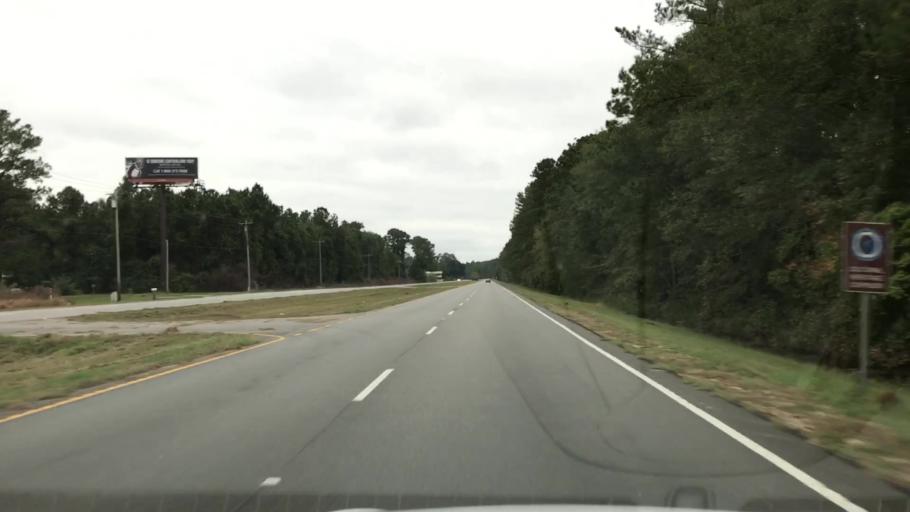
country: US
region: South Carolina
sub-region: Georgetown County
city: Georgetown
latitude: 33.2225
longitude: -79.3785
